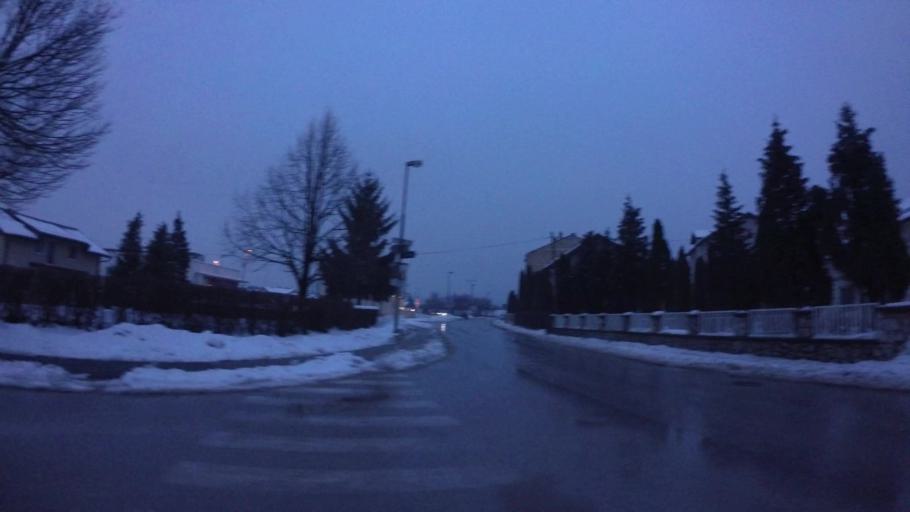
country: BA
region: Federation of Bosnia and Herzegovina
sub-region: Kanton Sarajevo
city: Sarajevo
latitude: 43.8371
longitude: 18.2989
